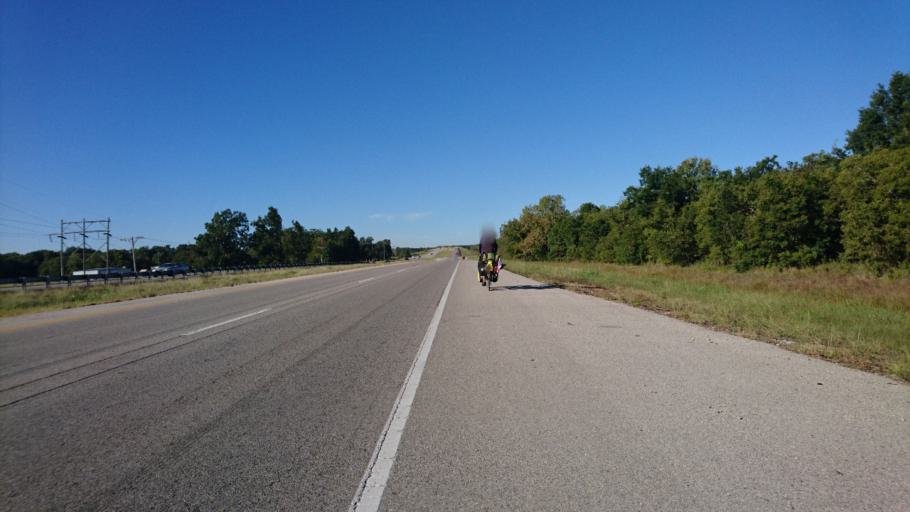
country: US
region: Oklahoma
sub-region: Rogers County
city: Verdigris
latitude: 36.2215
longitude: -95.7113
